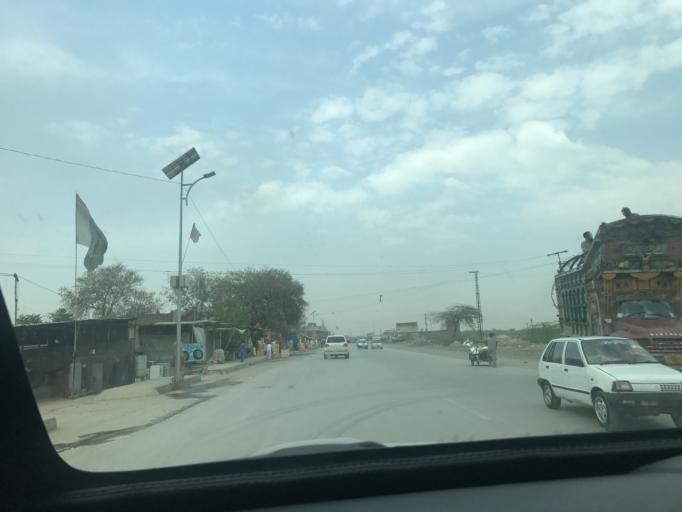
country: PK
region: Khyber Pakhtunkhwa
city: Peshawar
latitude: 33.9994
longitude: 71.4118
